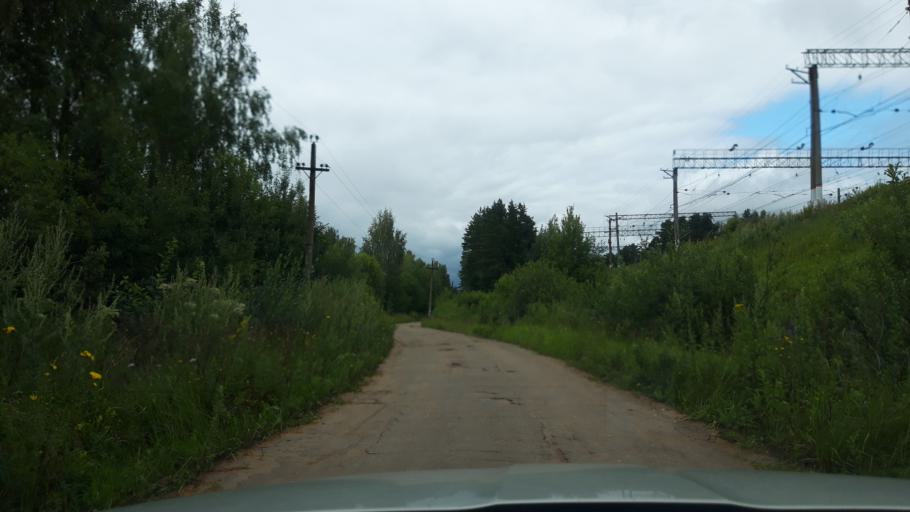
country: RU
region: Moskovskaya
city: Povarovo
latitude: 56.0537
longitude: 37.0578
